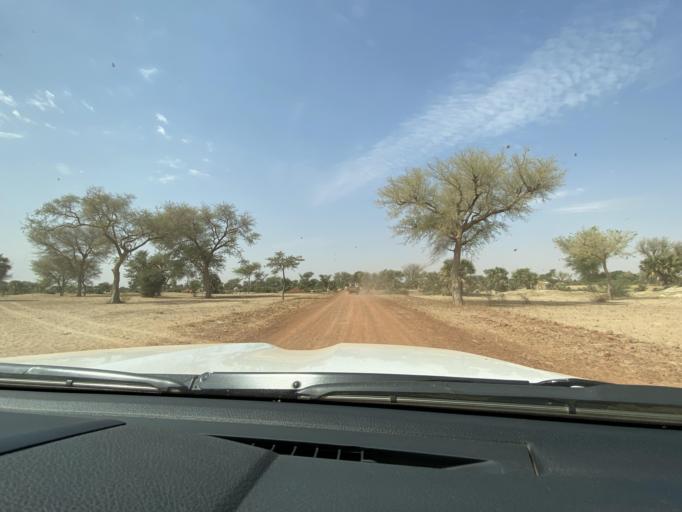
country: NE
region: Dosso
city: Birnin Gaoure
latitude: 13.2471
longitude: 2.8568
